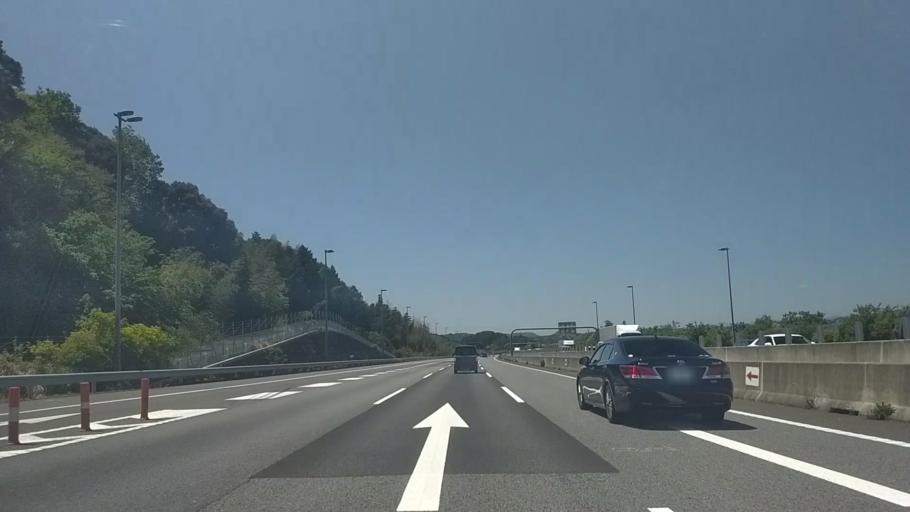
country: JP
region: Shizuoka
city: Mori
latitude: 34.8234
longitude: 137.9388
